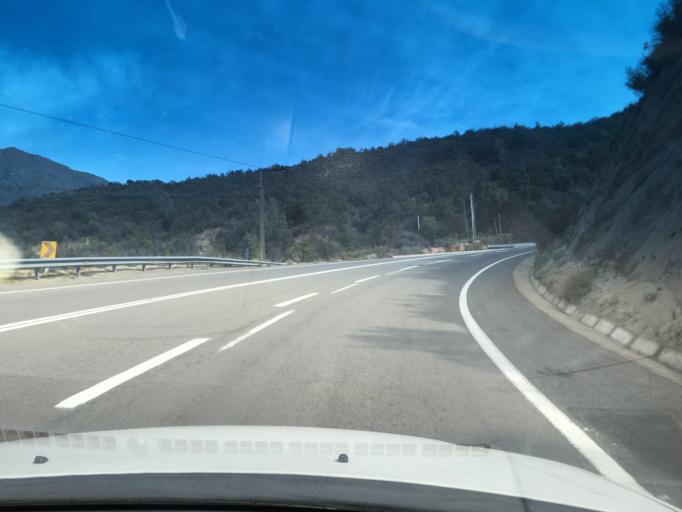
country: CL
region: Valparaiso
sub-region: Provincia de San Felipe
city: Llaillay
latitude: -33.0661
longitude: -70.9904
